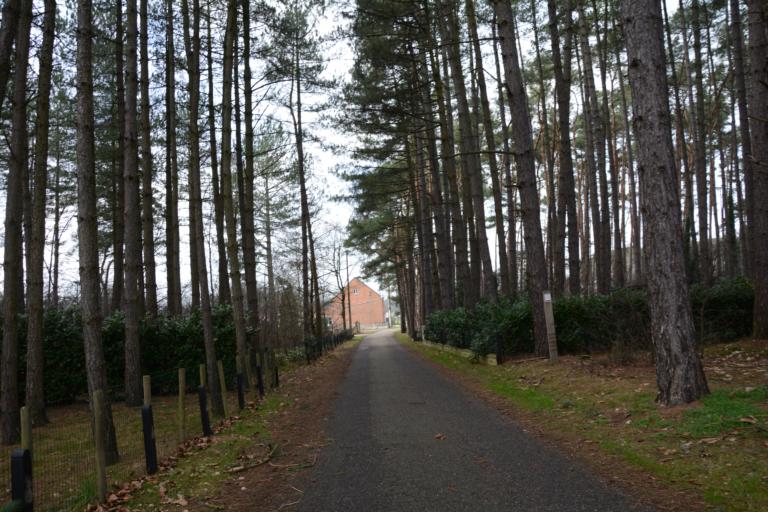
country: BE
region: Flanders
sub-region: Provincie Antwerpen
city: Herselt
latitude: 51.0485
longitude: 4.9176
